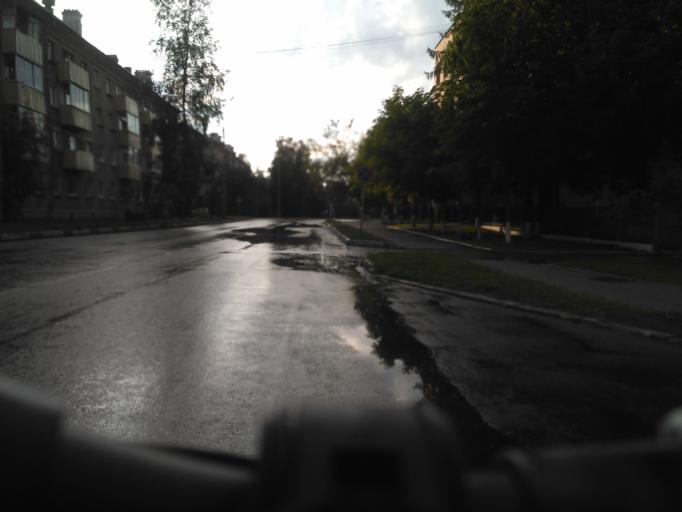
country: RU
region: Moskovskaya
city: Dubna
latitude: 56.7504
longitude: 37.2038
